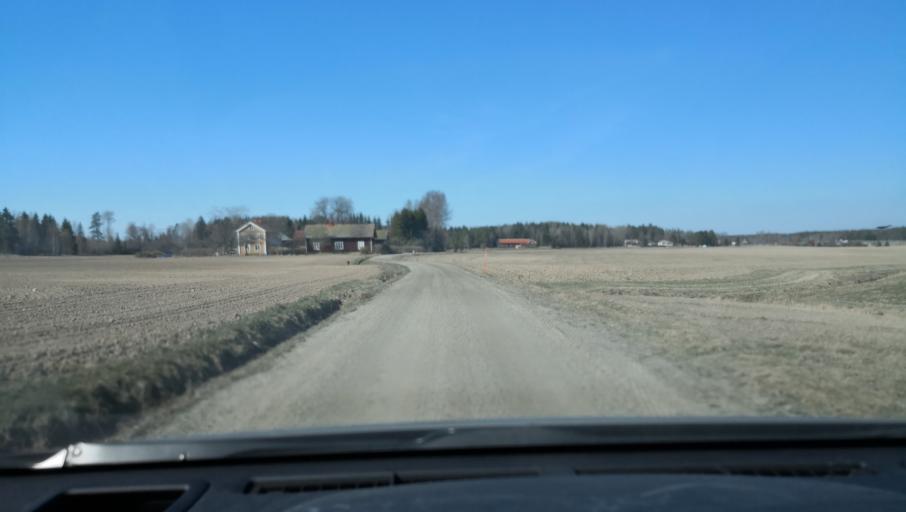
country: SE
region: Vaestmanland
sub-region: Sala Kommun
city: Sala
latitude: 59.8981
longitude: 16.5296
